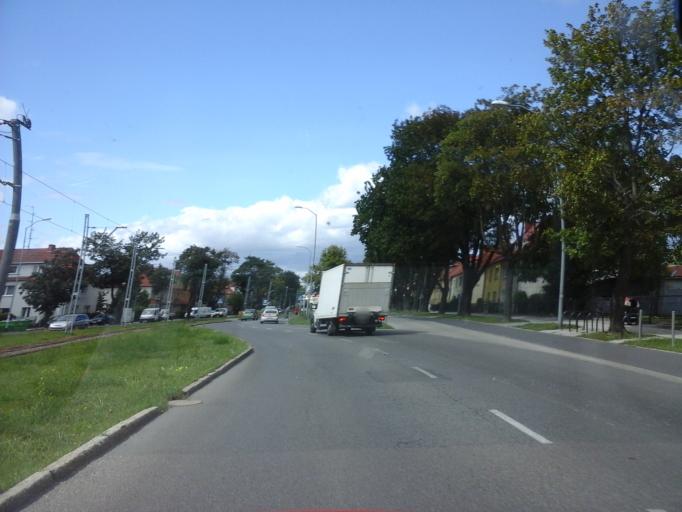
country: PL
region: West Pomeranian Voivodeship
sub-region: Powiat policki
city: Przeclaw
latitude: 53.4224
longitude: 14.4974
